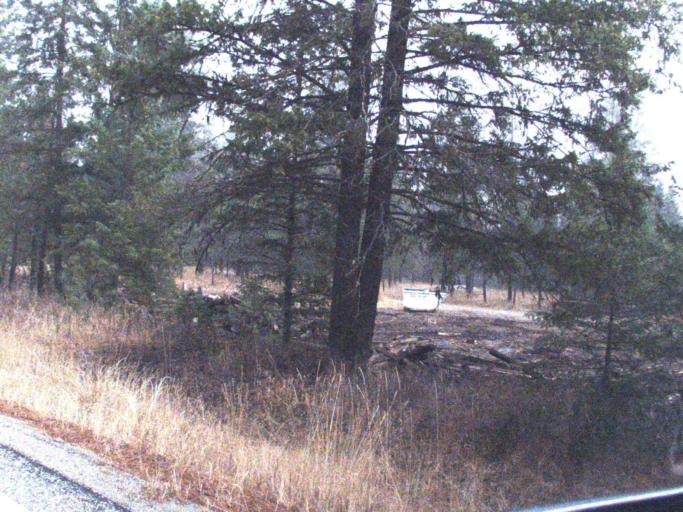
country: US
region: Washington
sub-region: Stevens County
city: Kettle Falls
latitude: 48.8513
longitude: -118.2010
